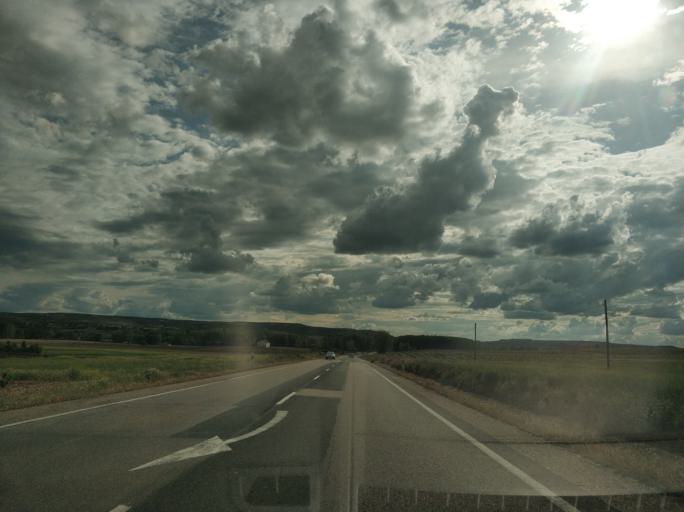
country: ES
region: Castille and Leon
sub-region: Provincia de Burgos
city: Haza
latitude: 41.6343
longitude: -3.8342
